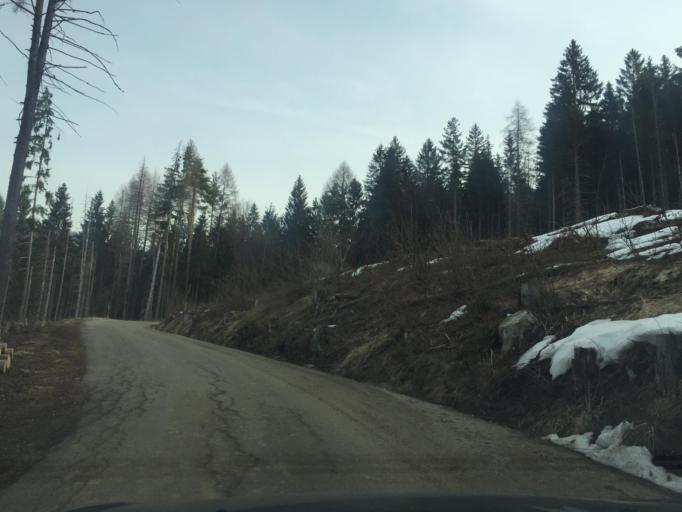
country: IT
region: Friuli Venezia Giulia
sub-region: Provincia di Udine
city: Tarvisio
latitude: 46.5021
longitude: 13.6365
